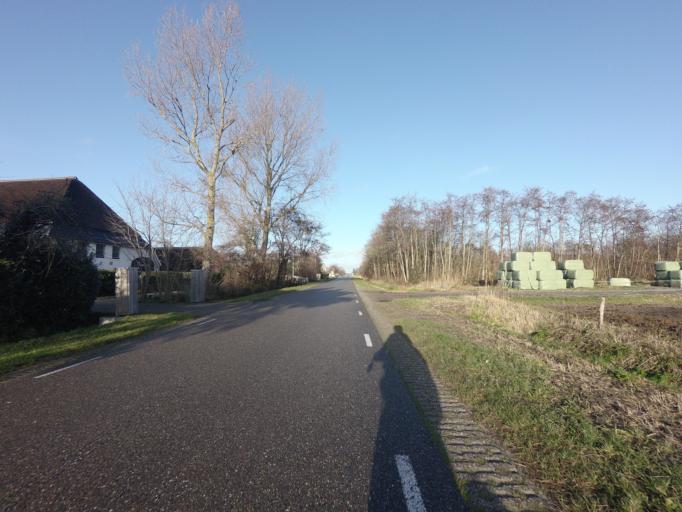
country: NL
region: North Holland
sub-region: Gemeente Texel
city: Den Burg
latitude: 53.1542
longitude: 4.8649
